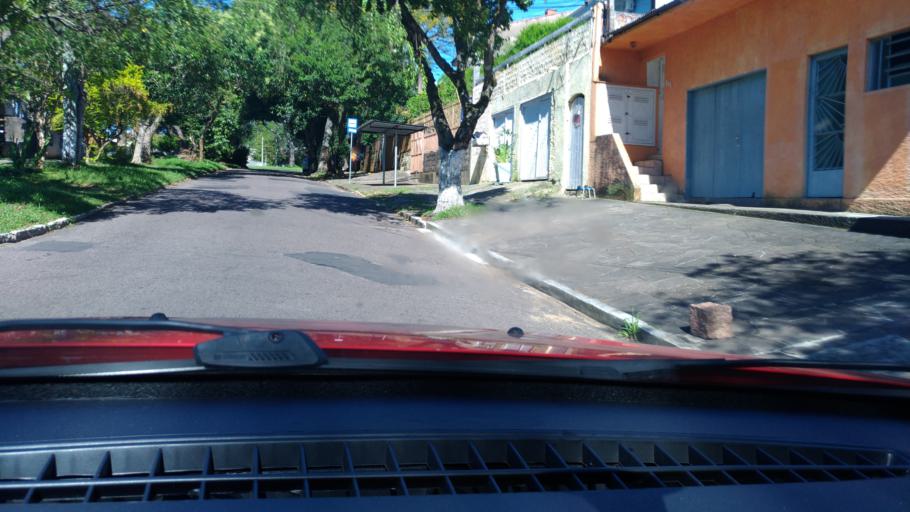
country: BR
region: Rio Grande do Sul
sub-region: Cachoeirinha
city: Cachoeirinha
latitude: -30.0327
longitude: -51.1293
